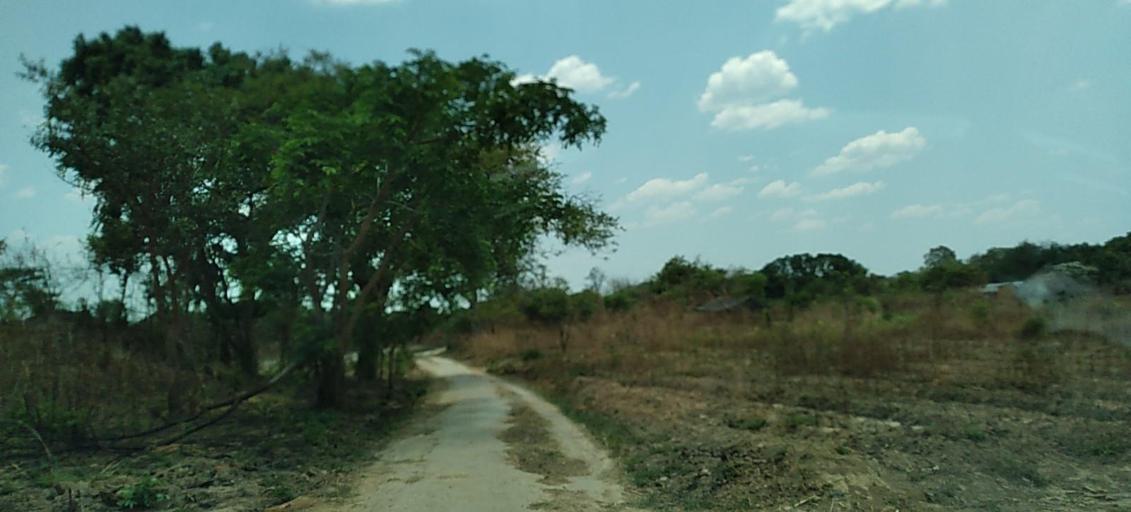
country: ZM
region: Copperbelt
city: Chililabombwe
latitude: -12.4633
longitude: 27.6690
